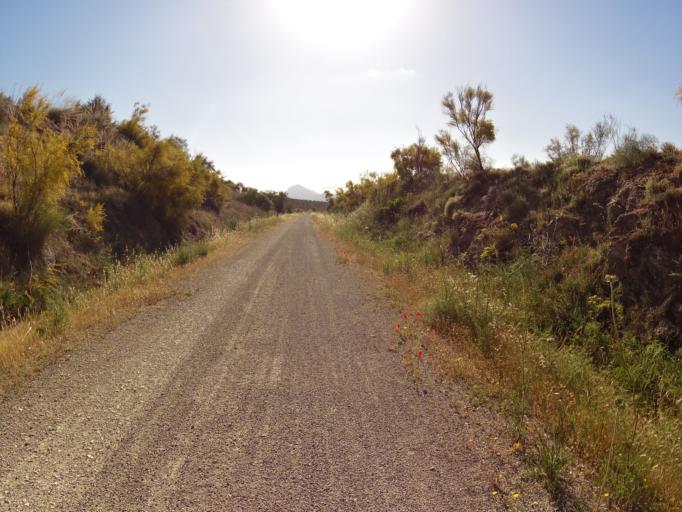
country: ES
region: Andalusia
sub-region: Province of Cordoba
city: Luque
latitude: 37.5829
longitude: -4.2076
